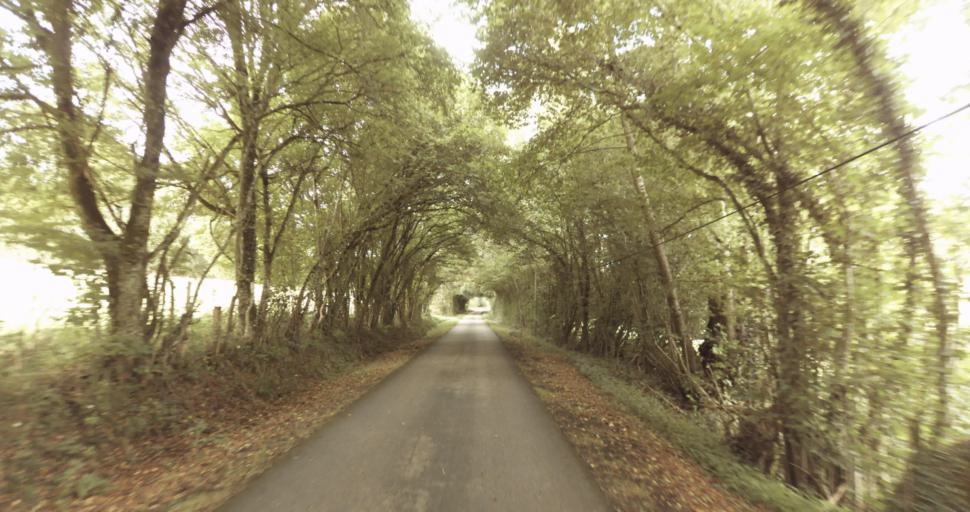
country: FR
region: Lower Normandy
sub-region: Departement de l'Orne
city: Gace
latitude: 48.7774
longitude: 0.3613
